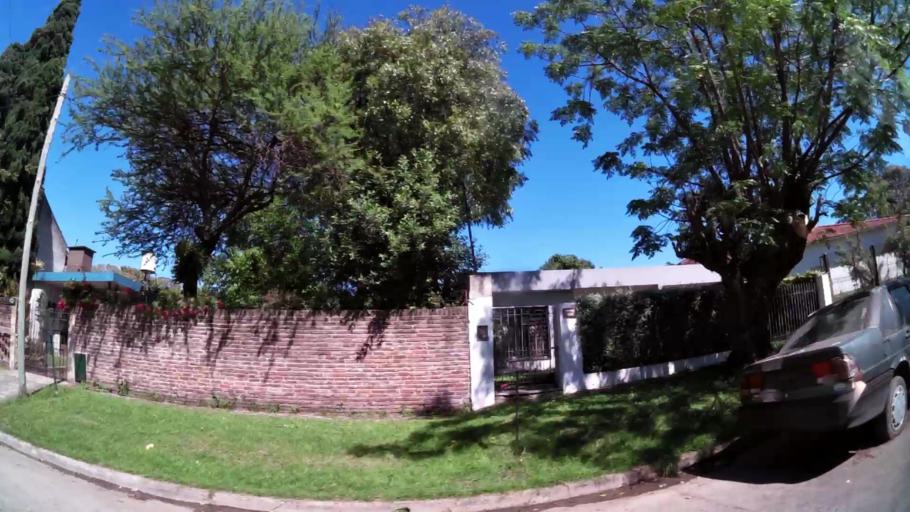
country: AR
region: Buenos Aires
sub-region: Partido de Tigre
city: Tigre
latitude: -34.5033
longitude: -58.6156
